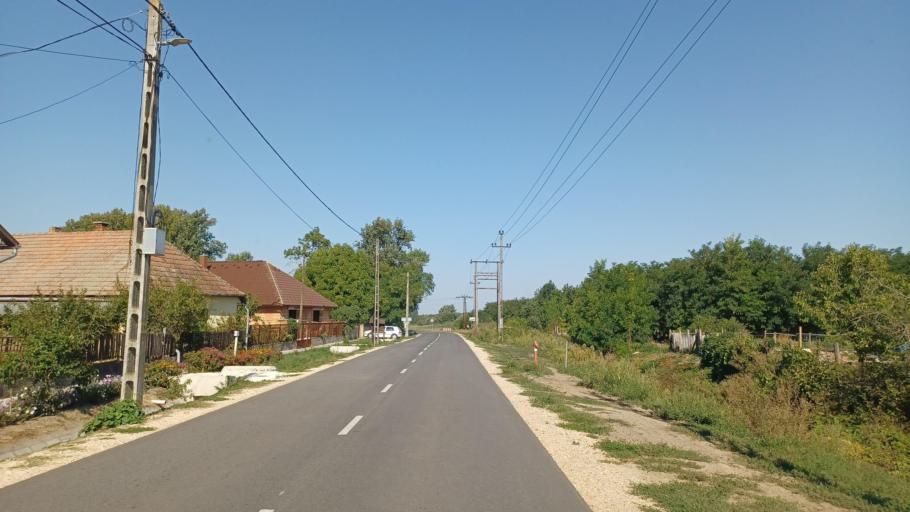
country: HU
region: Tolna
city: Nemetker
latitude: 46.7304
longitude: 18.7477
